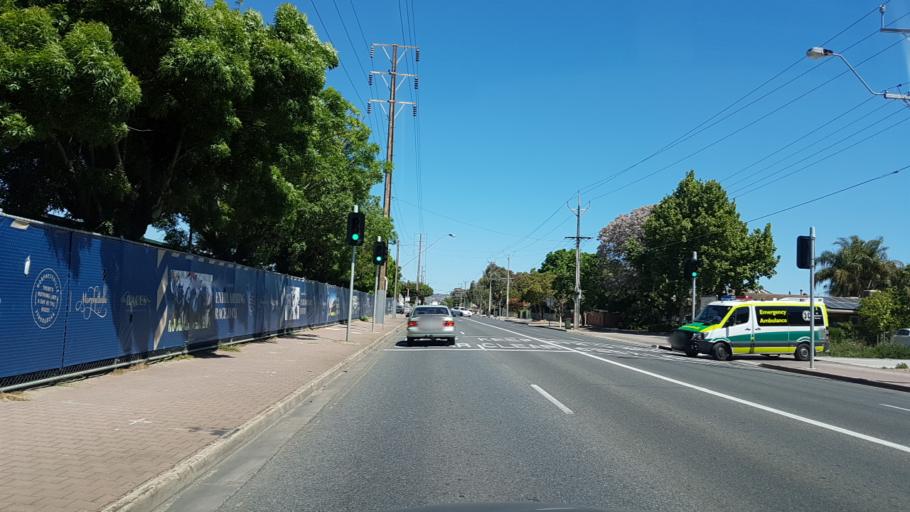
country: AU
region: South Australia
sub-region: Marion
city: Plympton Park
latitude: -34.9803
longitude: 138.5381
